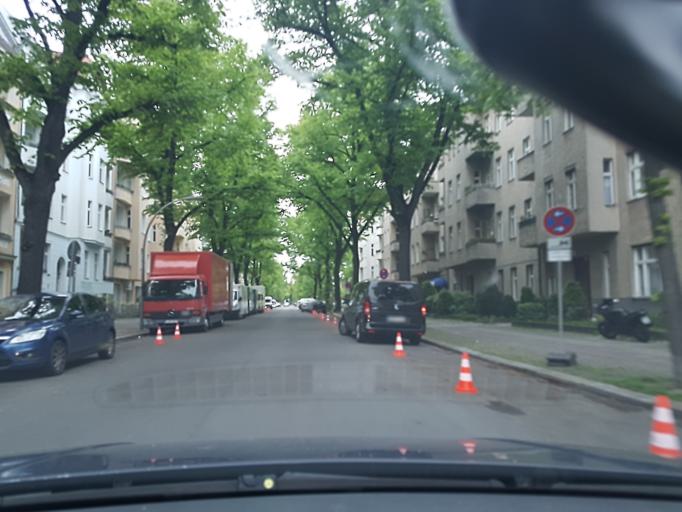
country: DE
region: Berlin
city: Tempelhof Bezirk
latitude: 52.4567
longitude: 13.3869
